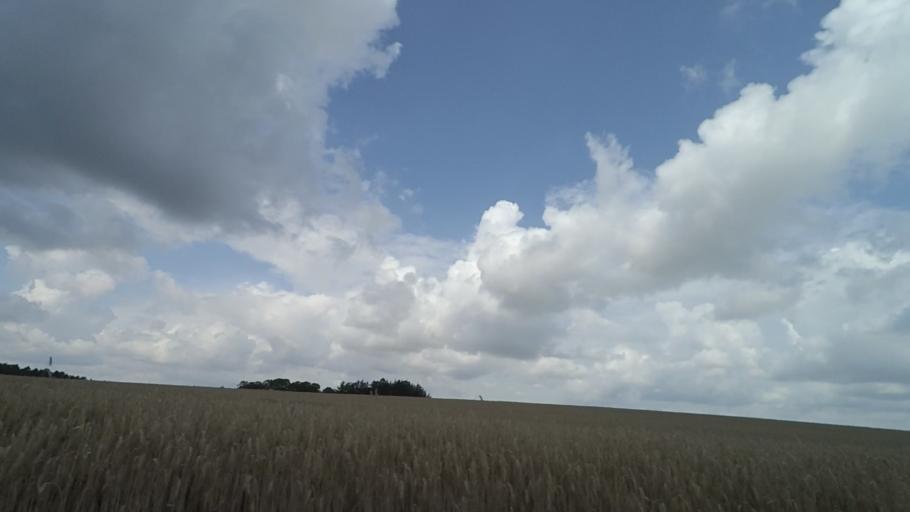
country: DK
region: Central Jutland
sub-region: Norddjurs Kommune
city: Allingabro
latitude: 56.4976
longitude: 10.3708
